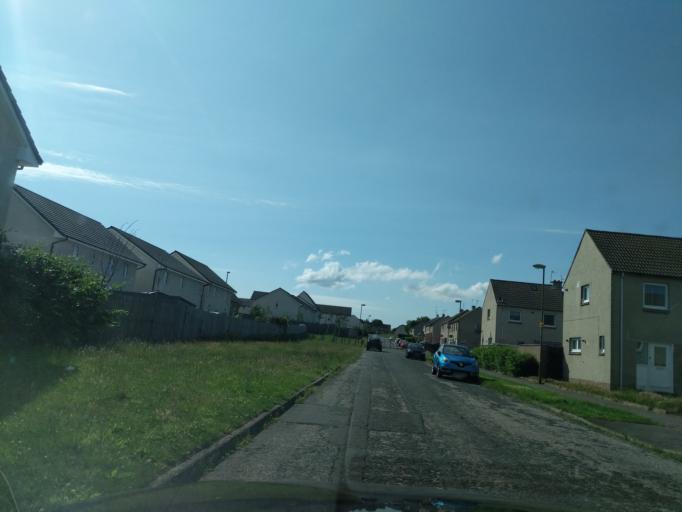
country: GB
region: Scotland
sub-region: Midlothian
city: Bonnyrigg
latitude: 55.8693
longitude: -3.1003
